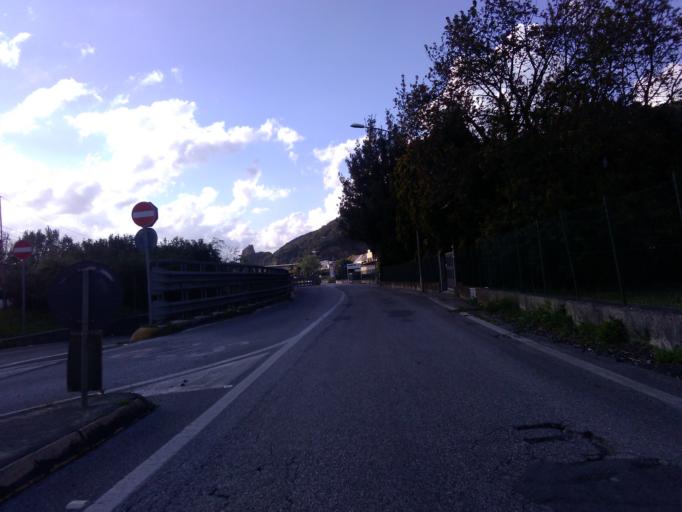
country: IT
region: Tuscany
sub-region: Provincia di Lucca
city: Strettoia
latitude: 43.9910
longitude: 10.1816
